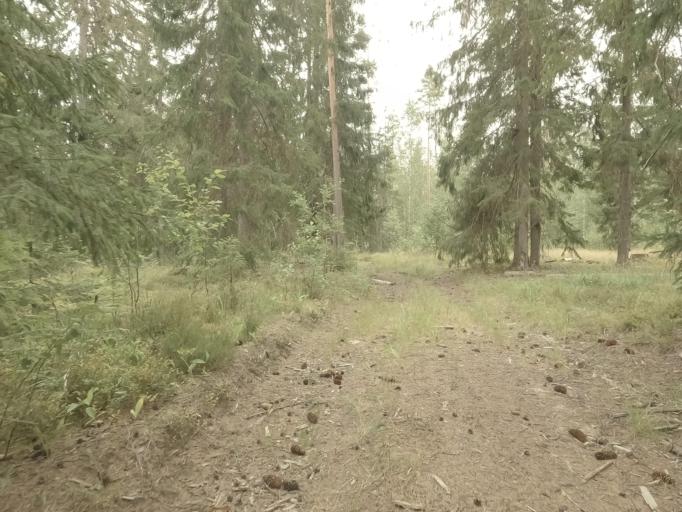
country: RU
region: Leningrad
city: Kamennogorsk
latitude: 61.0477
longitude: 29.1848
